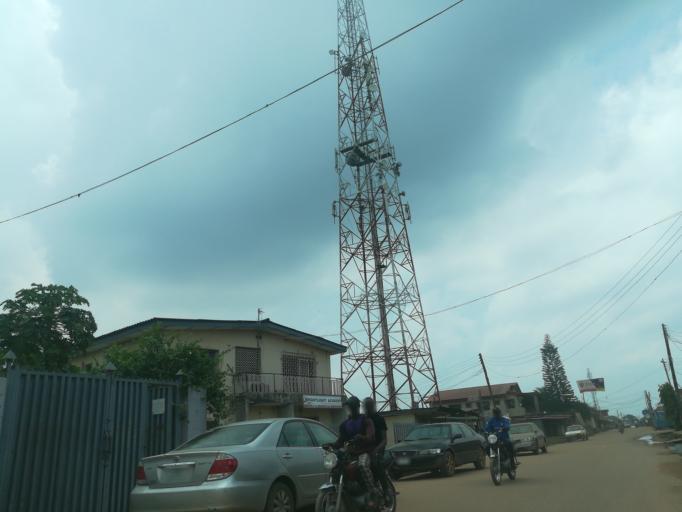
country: NG
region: Lagos
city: Ikorodu
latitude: 6.6207
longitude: 3.5207
